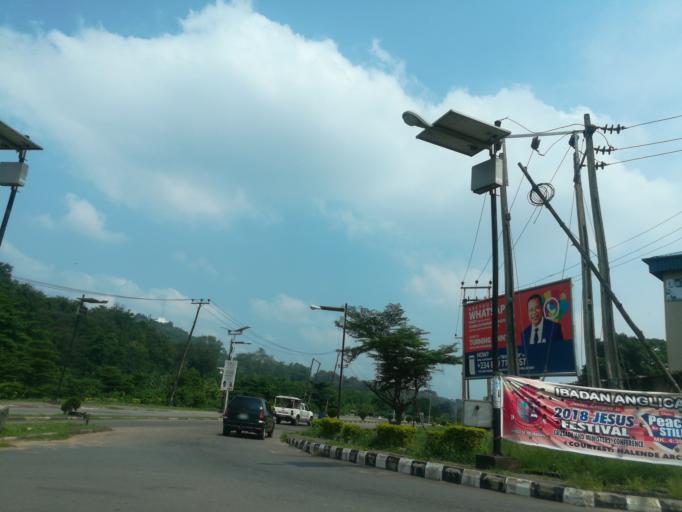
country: NG
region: Oyo
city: Ibadan
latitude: 7.4014
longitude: 3.8971
